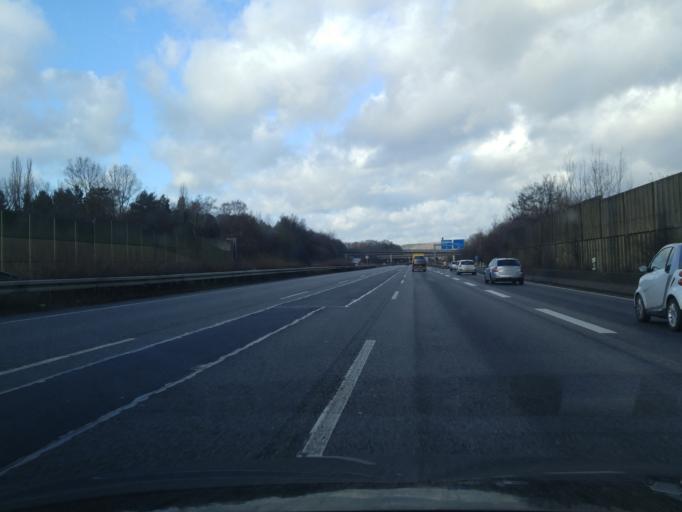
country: DE
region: Hesse
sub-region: Regierungsbezirk Kassel
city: Lohfelden
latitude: 51.3037
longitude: 9.5616
